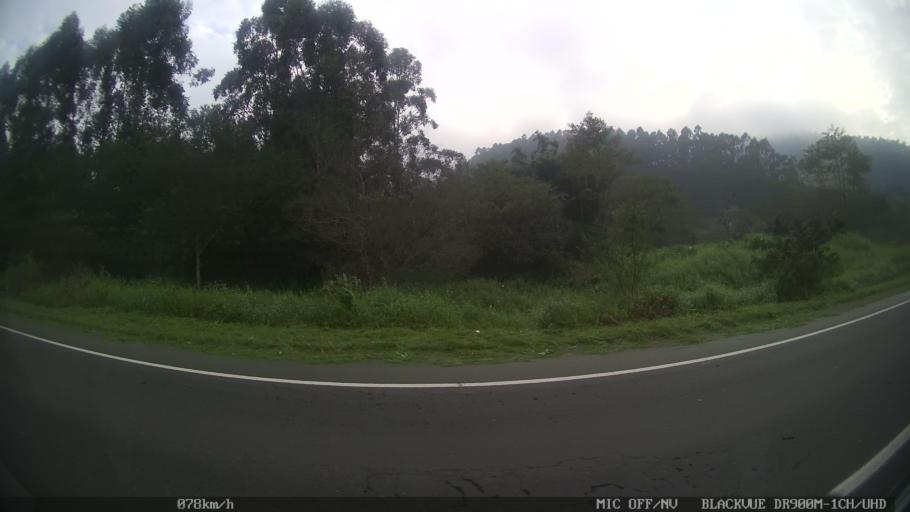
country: BR
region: Santa Catarina
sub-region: Penha
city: Penha
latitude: -26.8093
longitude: -48.6710
